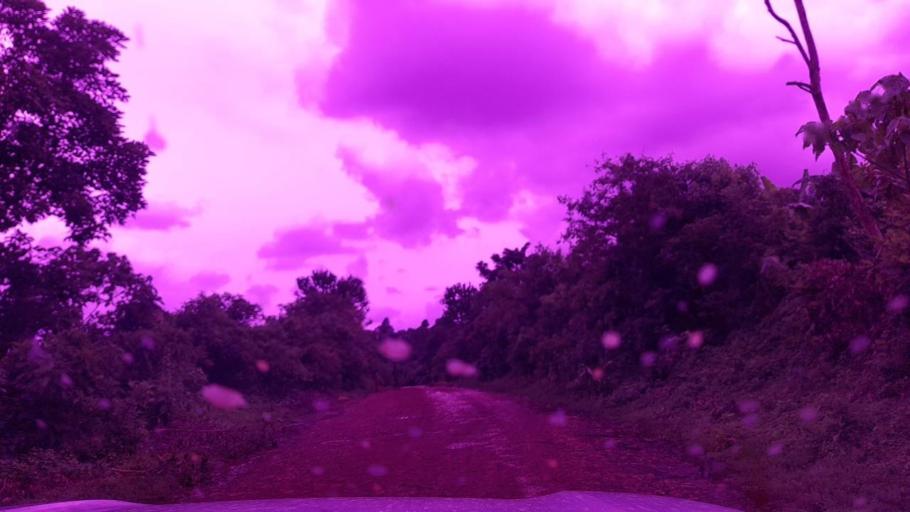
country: ET
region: Southern Nations, Nationalities, and People's Region
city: Tippi
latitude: 7.5828
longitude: 35.6700
